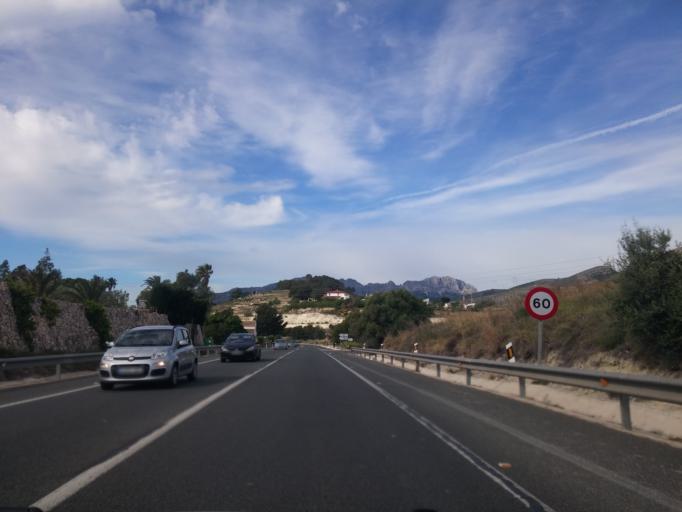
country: ES
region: Valencia
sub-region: Provincia de Alicante
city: Benissa
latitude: 38.7112
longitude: 0.0404
